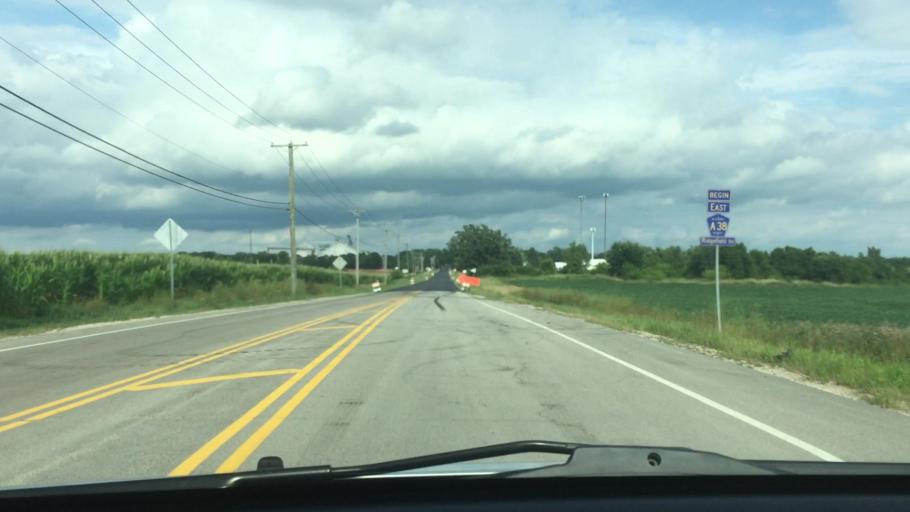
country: US
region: Illinois
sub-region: McHenry County
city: Lakewood
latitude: 42.2677
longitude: -88.3769
